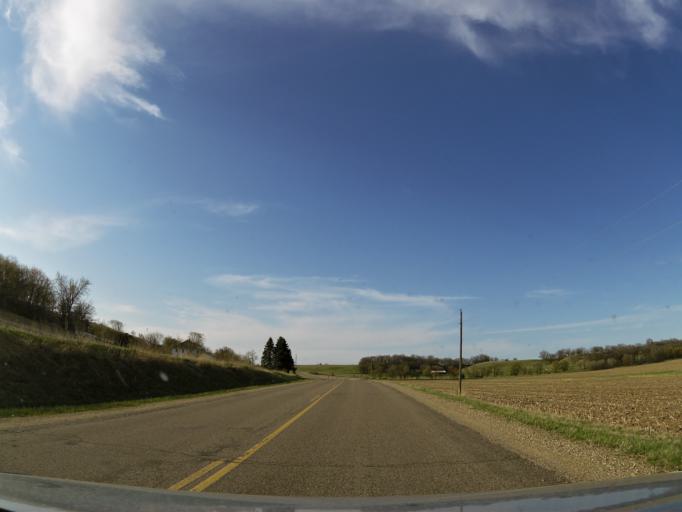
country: US
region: Wisconsin
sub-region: Pierce County
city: River Falls
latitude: 44.7786
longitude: -92.6397
